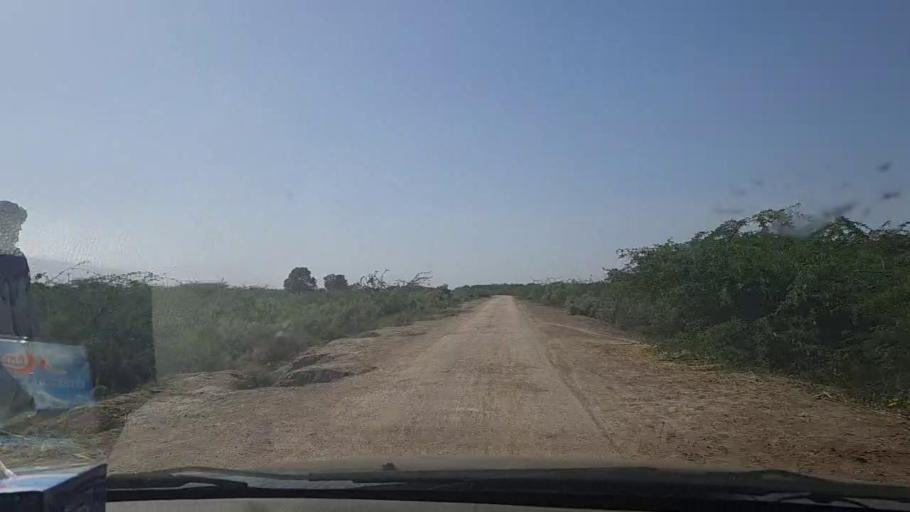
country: PK
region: Sindh
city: Chuhar Jamali
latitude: 24.2945
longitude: 67.7607
